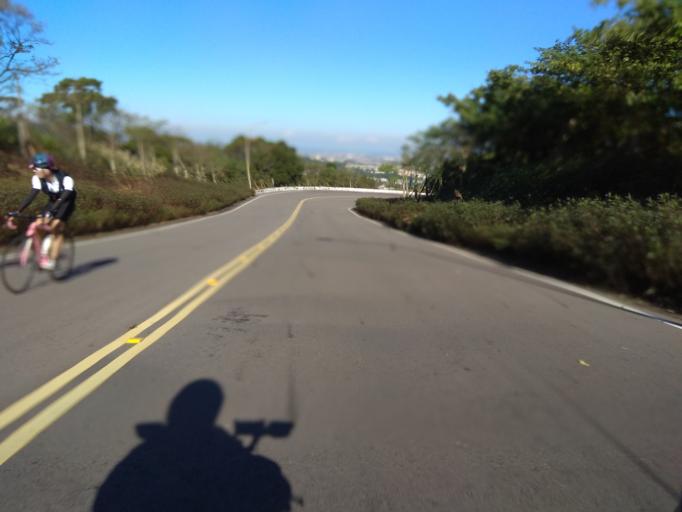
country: TW
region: Taiwan
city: Daxi
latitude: 24.8915
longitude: 121.1476
